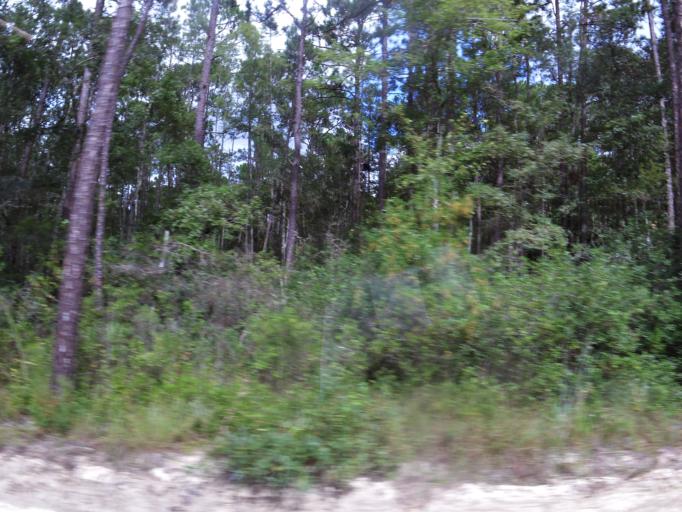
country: US
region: Florida
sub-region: Nassau County
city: Hilliard
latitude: 30.6082
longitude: -82.0766
